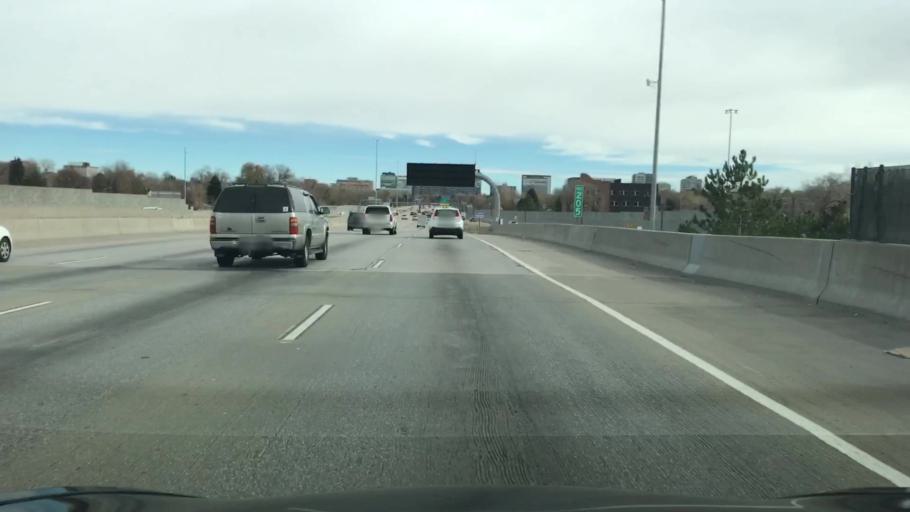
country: US
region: Colorado
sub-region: Arapahoe County
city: Glendale
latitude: 39.6845
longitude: -104.9590
